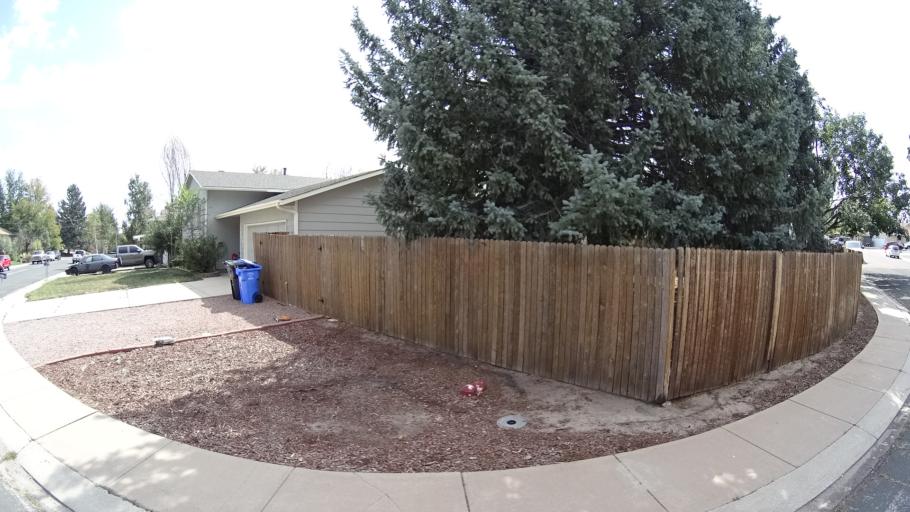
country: US
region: Colorado
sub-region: El Paso County
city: Cimarron Hills
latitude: 38.8633
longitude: -104.7609
